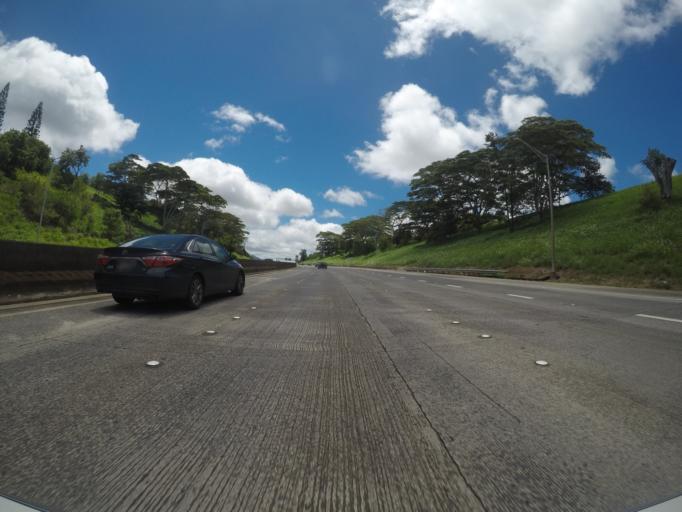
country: US
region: Hawaii
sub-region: Honolulu County
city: Mililani Town
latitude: 21.4612
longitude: -157.9958
